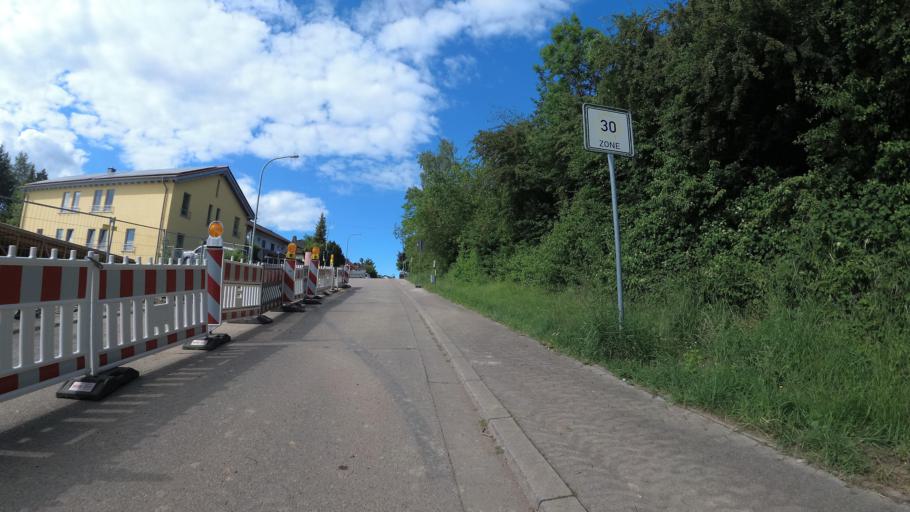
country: DE
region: Saarland
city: Riegelsberg
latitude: 49.3084
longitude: 6.9085
